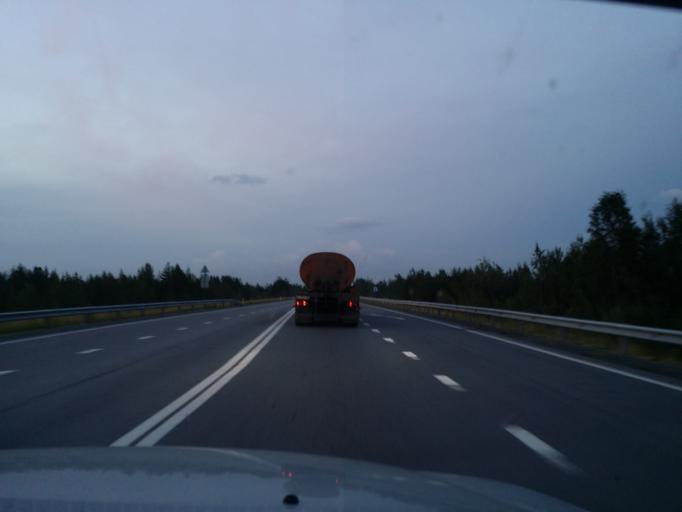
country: RU
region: Khanty-Mansiyskiy Avtonomnyy Okrug
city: Poykovskiy
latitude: 61.3526
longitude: 73.2929
